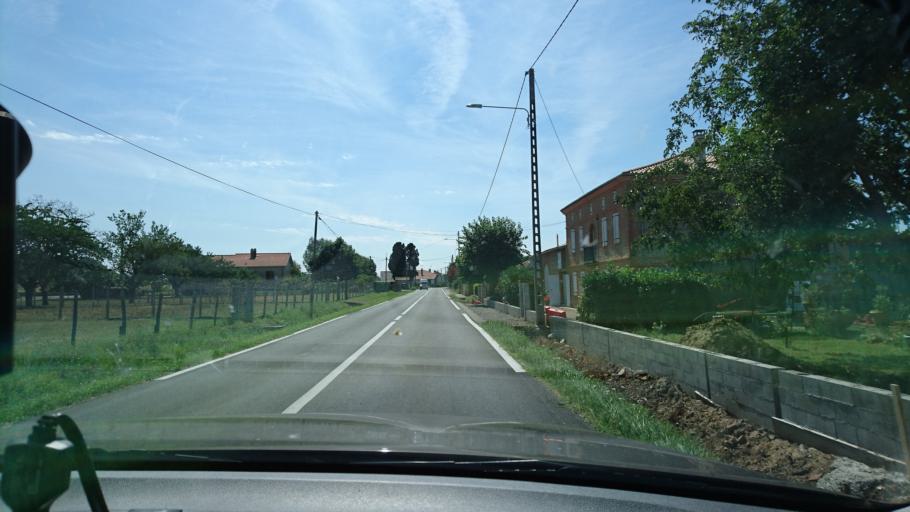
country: FR
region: Midi-Pyrenees
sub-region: Departement de la Haute-Garonne
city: Noe
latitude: 43.3387
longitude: 1.2635
